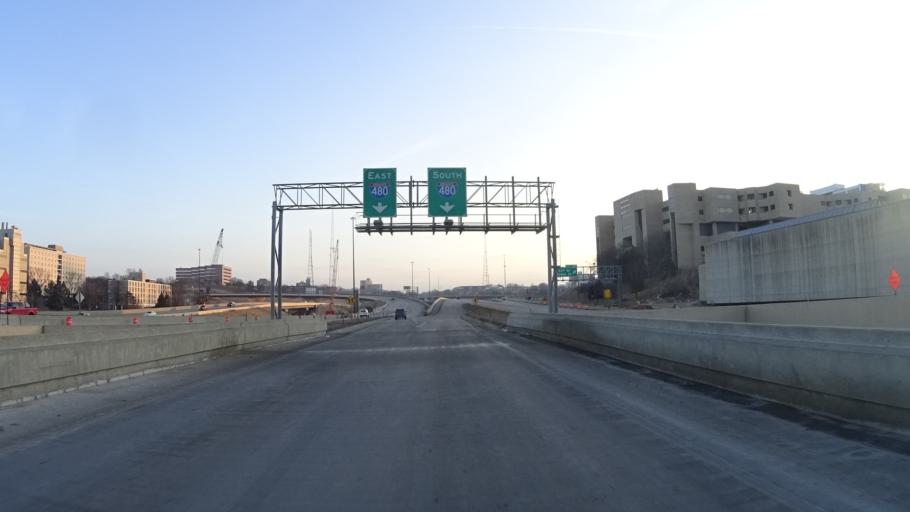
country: US
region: Nebraska
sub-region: Douglas County
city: Omaha
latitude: 41.2669
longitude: -95.9527
